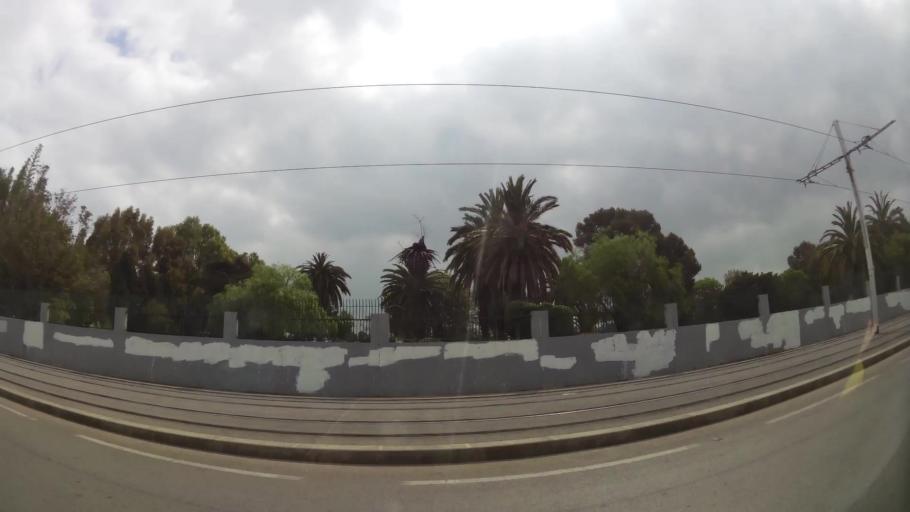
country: MA
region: Rabat-Sale-Zemmour-Zaer
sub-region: Rabat
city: Rabat
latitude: 34.0057
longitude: -6.8437
